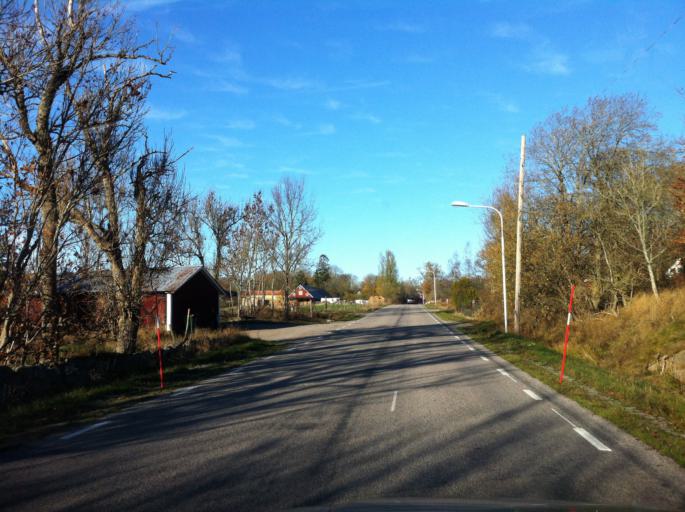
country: SE
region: Blekinge
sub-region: Ronneby Kommun
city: Brakne-Hoby
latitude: 56.1803
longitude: 15.1235
